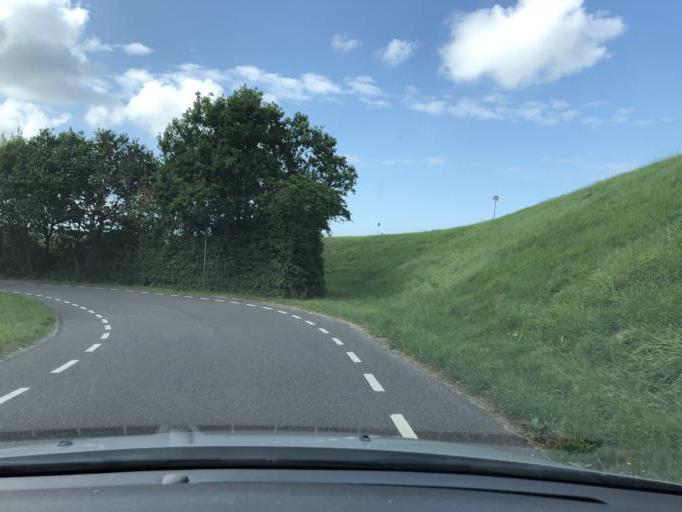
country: NL
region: Zeeland
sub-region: Gemeente Reimerswaal
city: Yerseke
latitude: 51.5024
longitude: 4.0519
